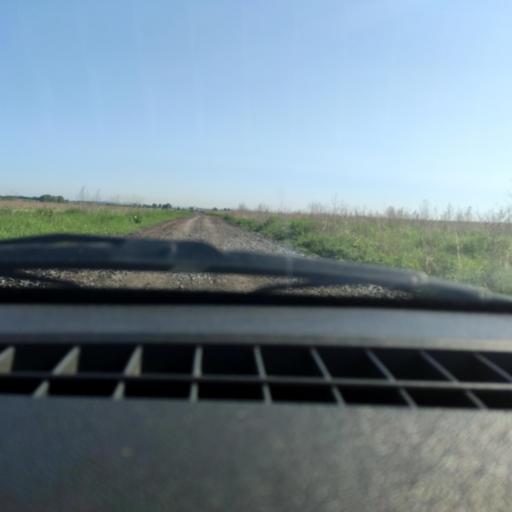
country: RU
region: Bashkortostan
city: Avdon
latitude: 54.5635
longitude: 55.8289
